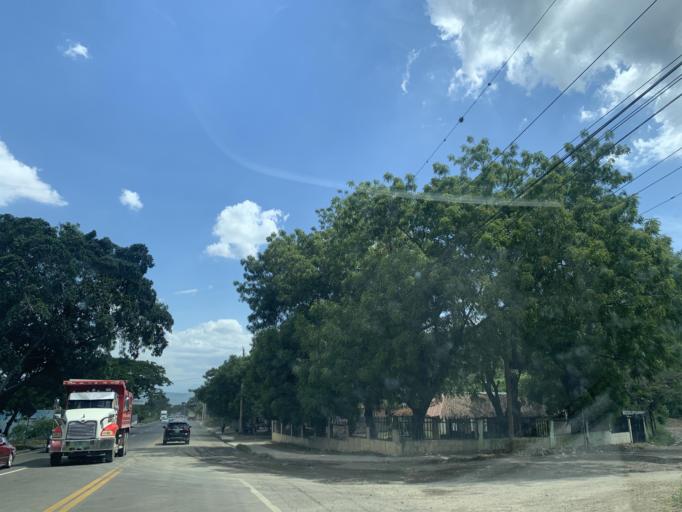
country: DO
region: Santiago
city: Villa Bisono
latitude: 19.5933
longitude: -70.8445
